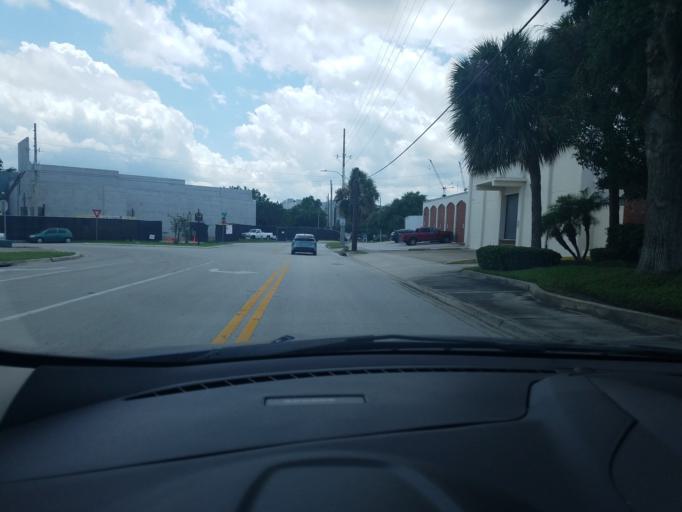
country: US
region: Florida
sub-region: Orange County
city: Fairview Shores
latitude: 28.5711
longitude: -81.3710
